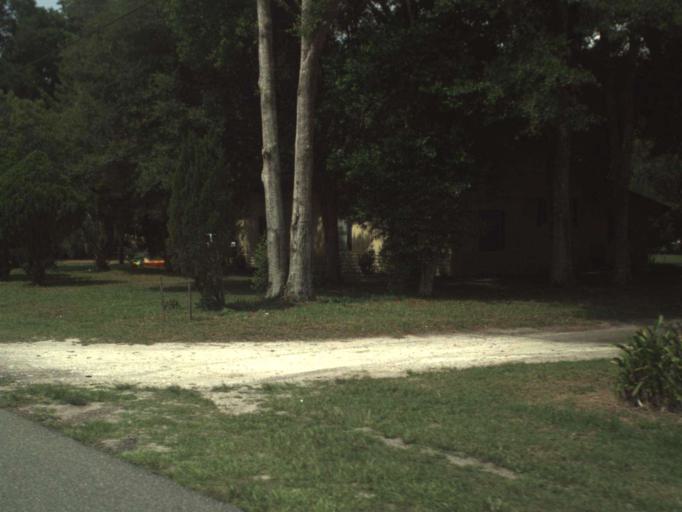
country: US
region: Florida
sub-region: Sumter County
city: Bushnell
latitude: 28.7030
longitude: -82.1043
